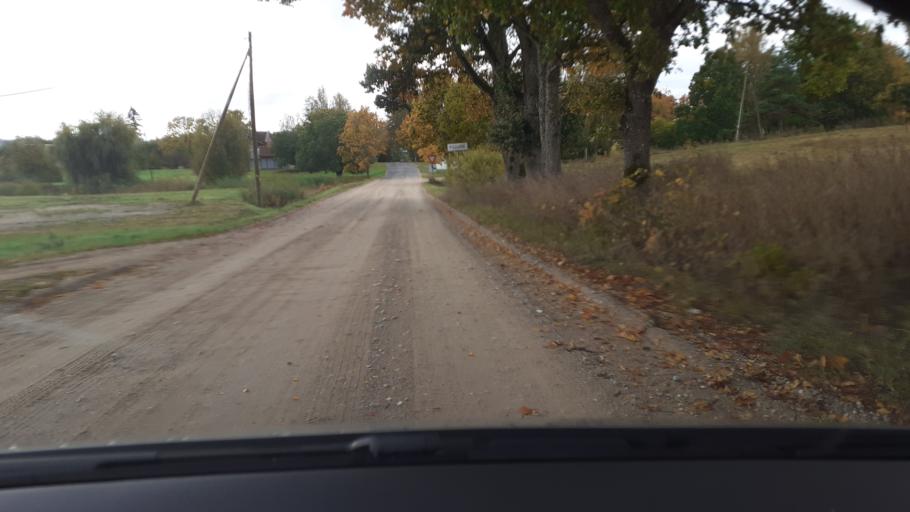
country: LV
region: Kuldigas Rajons
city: Kuldiga
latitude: 57.0212
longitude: 21.9135
